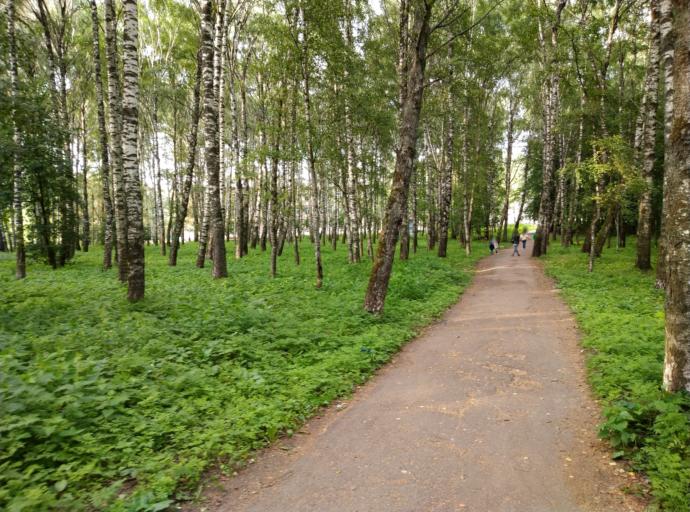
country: RU
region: Kostroma
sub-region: Kostromskoy Rayon
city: Kostroma
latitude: 57.7618
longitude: 40.9641
